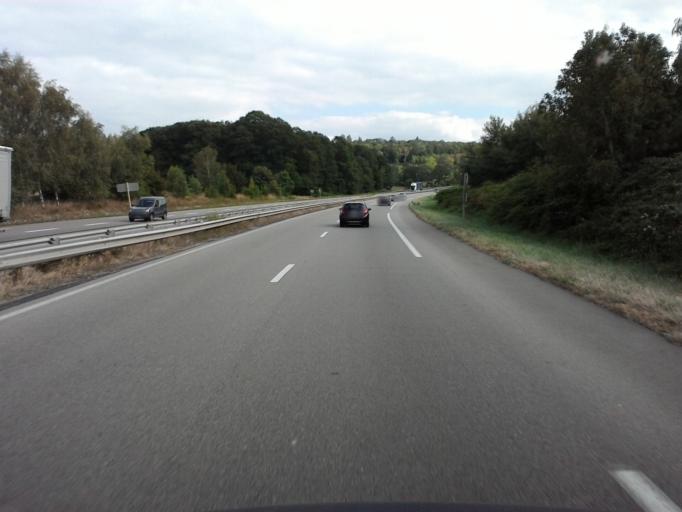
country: FR
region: Lorraine
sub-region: Departement des Vosges
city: Epinal
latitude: 48.1837
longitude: 6.4835
